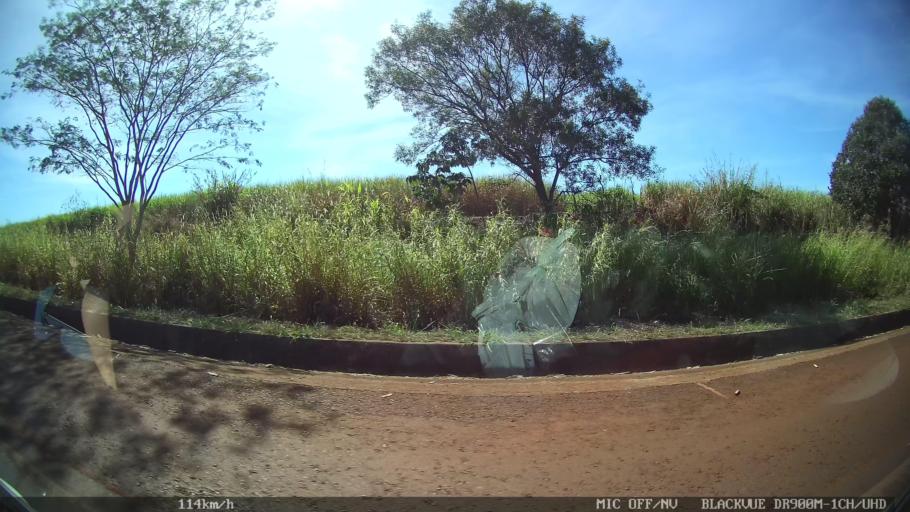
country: BR
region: Sao Paulo
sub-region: Sao Joaquim Da Barra
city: Sao Joaquim da Barra
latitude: -20.5386
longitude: -47.8214
